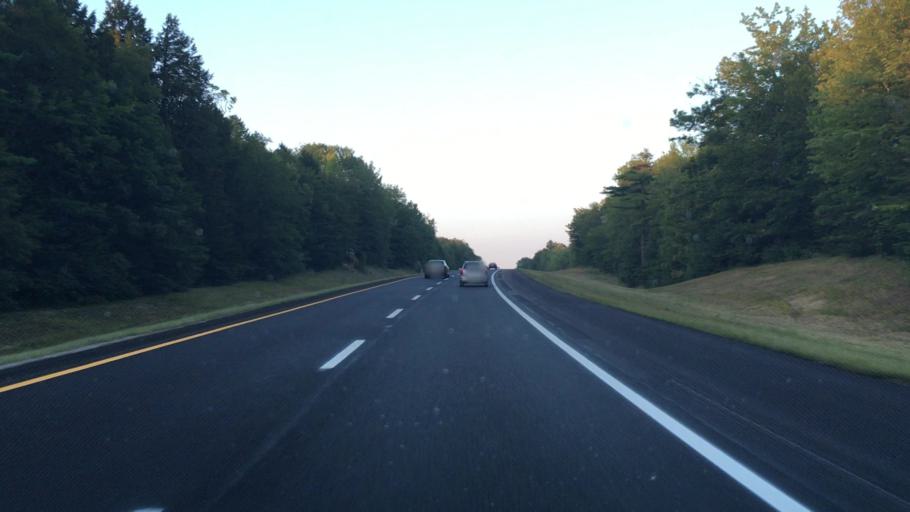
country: US
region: Maine
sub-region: Sagadahoc County
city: Topsham
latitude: 43.9942
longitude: -69.9367
